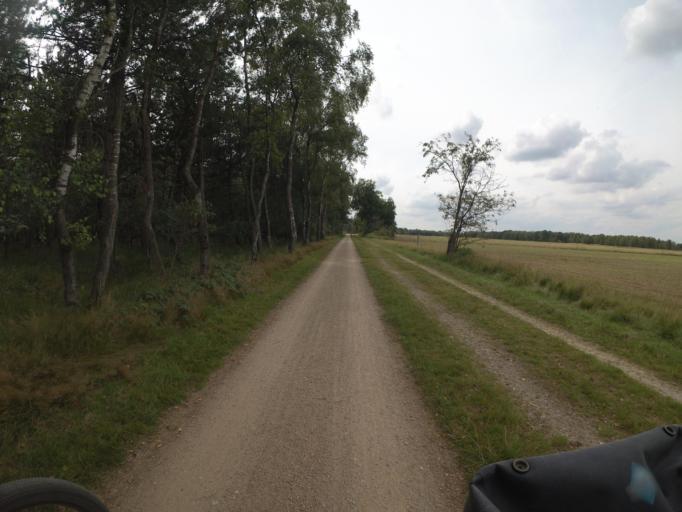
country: NL
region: Limburg
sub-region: Gemeente Bergen
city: Wellerlooi
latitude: 51.5893
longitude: 6.1076
